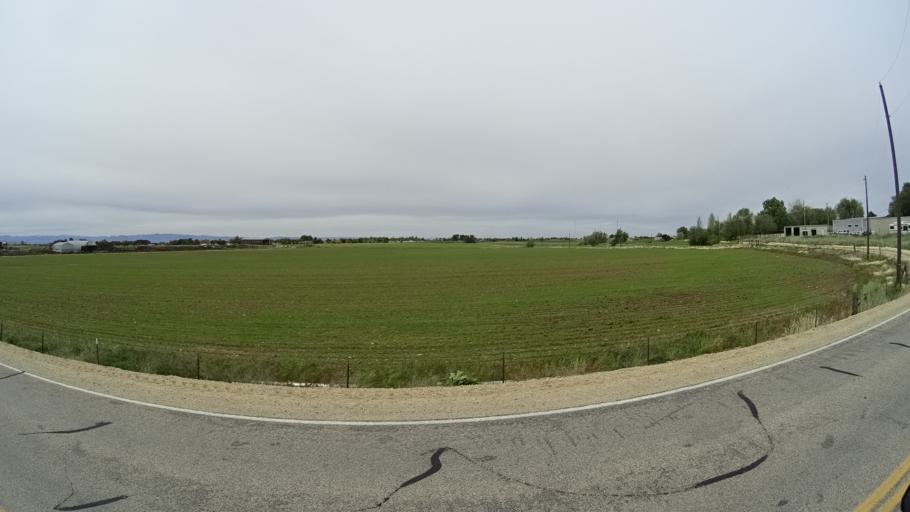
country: US
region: Idaho
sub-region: Ada County
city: Meridian
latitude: 43.5530
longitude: -116.3743
